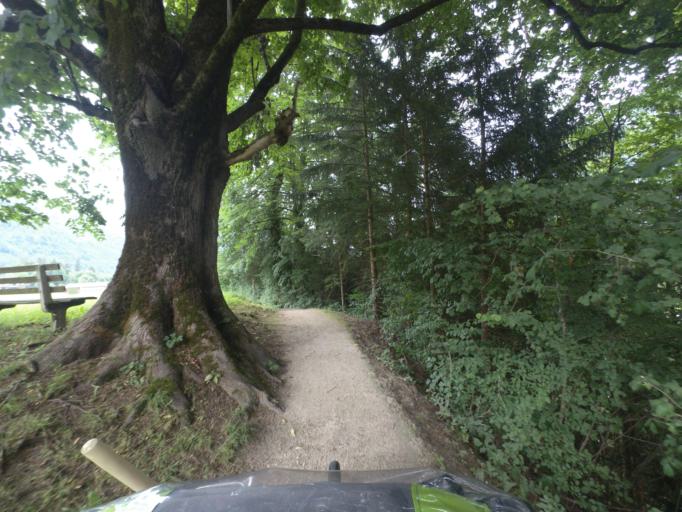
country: AT
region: Salzburg
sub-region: Politischer Bezirk Zell am See
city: Unken
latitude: 47.6515
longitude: 12.7281
